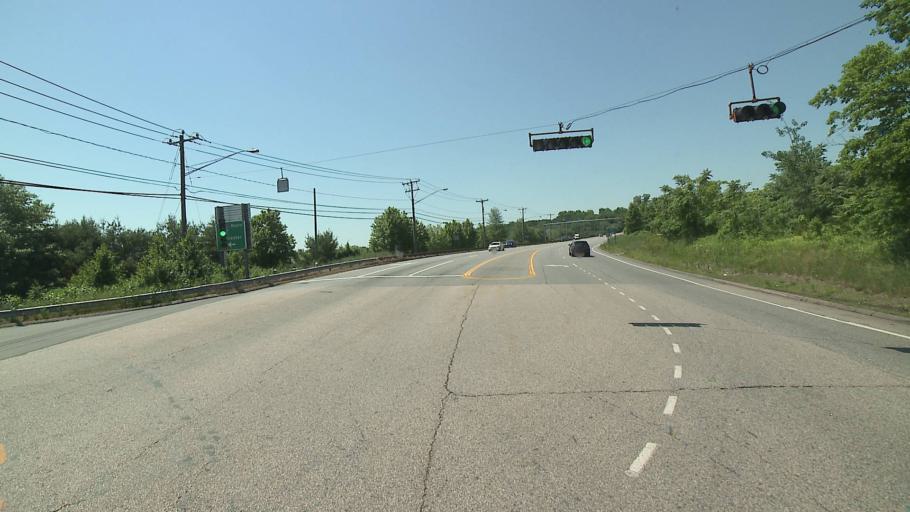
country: US
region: Connecticut
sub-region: New London County
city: Jewett City
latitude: 41.5882
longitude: -71.9911
